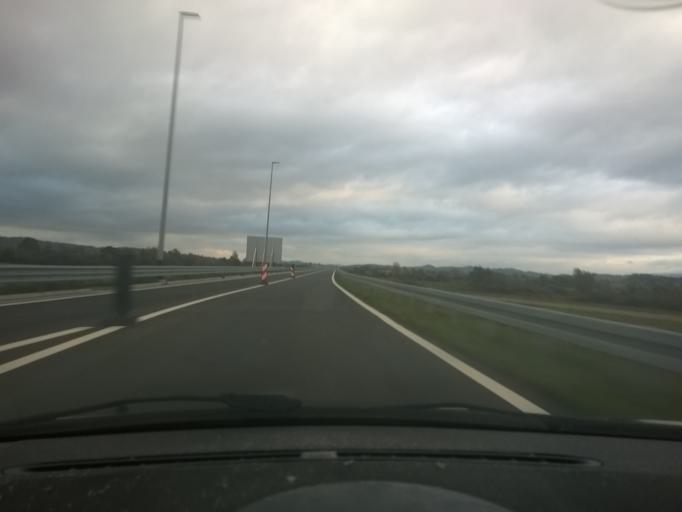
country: HR
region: Krapinsko-Zagorska
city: Oroslavje
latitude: 46.0062
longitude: 15.8874
